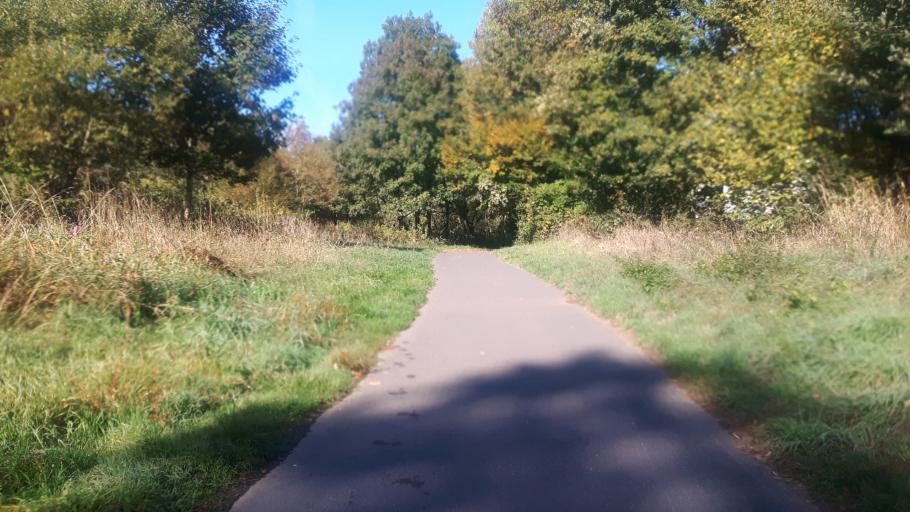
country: DE
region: Rheinland-Pfalz
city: Niederirsen
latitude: 50.8048
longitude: 7.5924
